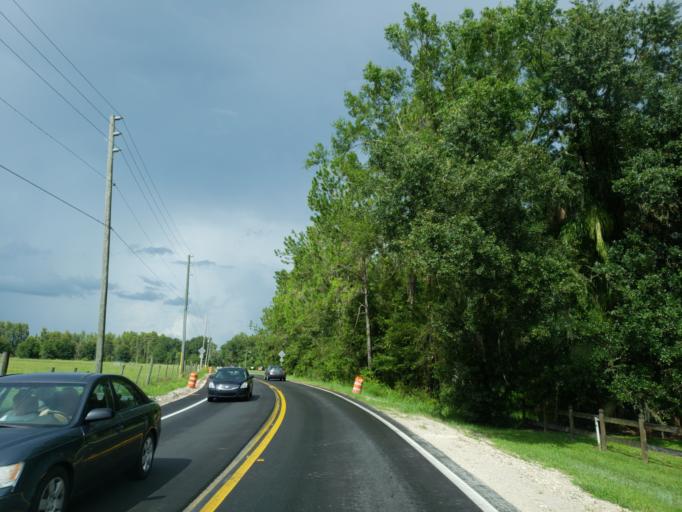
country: US
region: Florida
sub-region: Pasco County
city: Land O' Lakes
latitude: 28.2445
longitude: -82.4539
